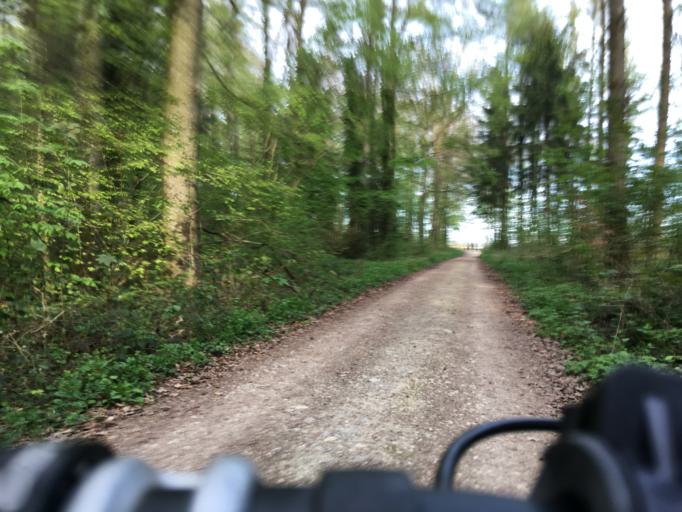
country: DE
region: Baden-Wuerttemberg
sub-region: Freiburg Region
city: Gottmadingen
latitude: 47.7402
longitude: 8.7543
